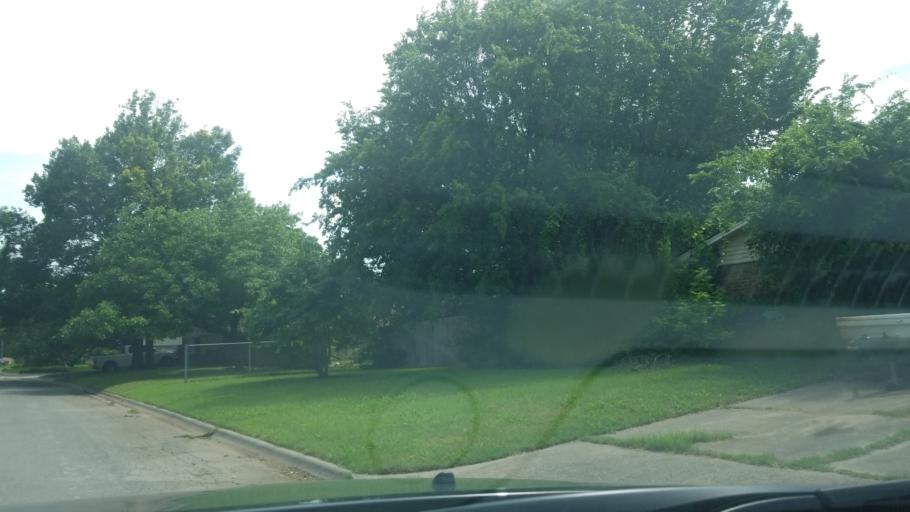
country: US
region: Texas
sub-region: Denton County
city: Denton
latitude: 33.2360
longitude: -97.1494
